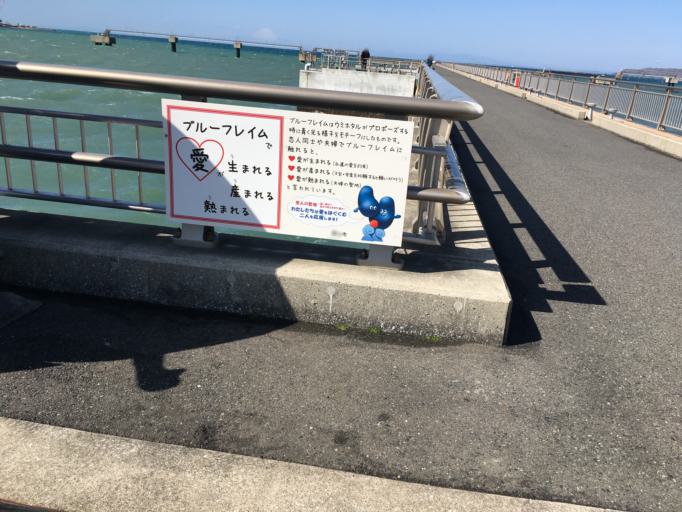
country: JP
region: Chiba
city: Tateyama
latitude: 34.9913
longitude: 139.8529
